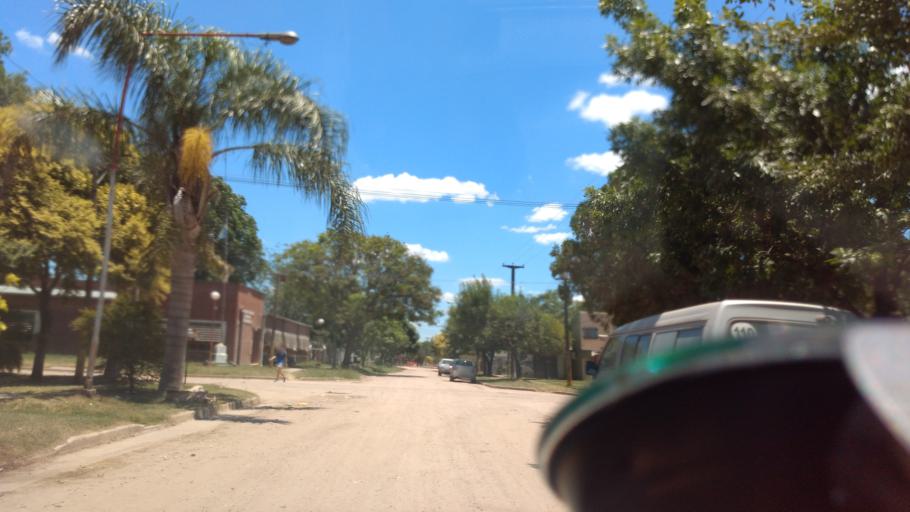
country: AR
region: Santa Fe
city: Laguna Paiva
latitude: -31.3117
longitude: -60.6631
